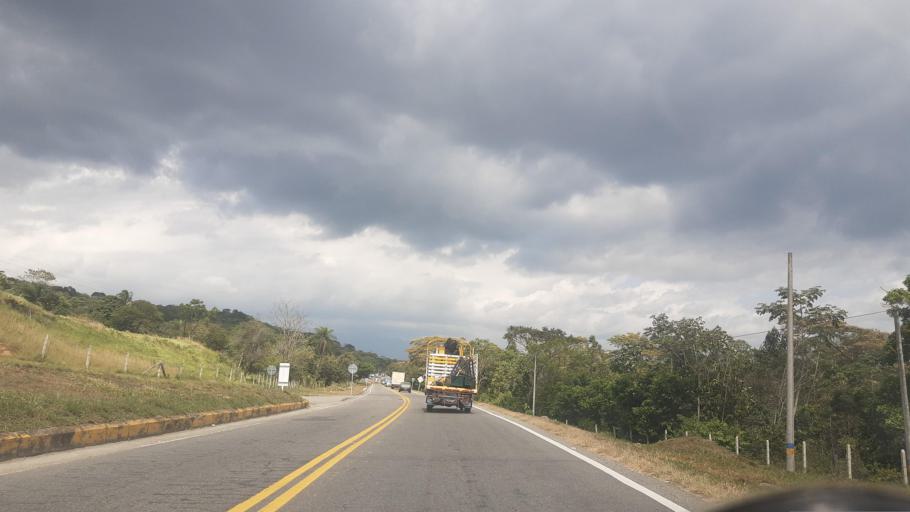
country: CO
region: Casanare
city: Tauramena
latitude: 4.9975
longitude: -72.6857
